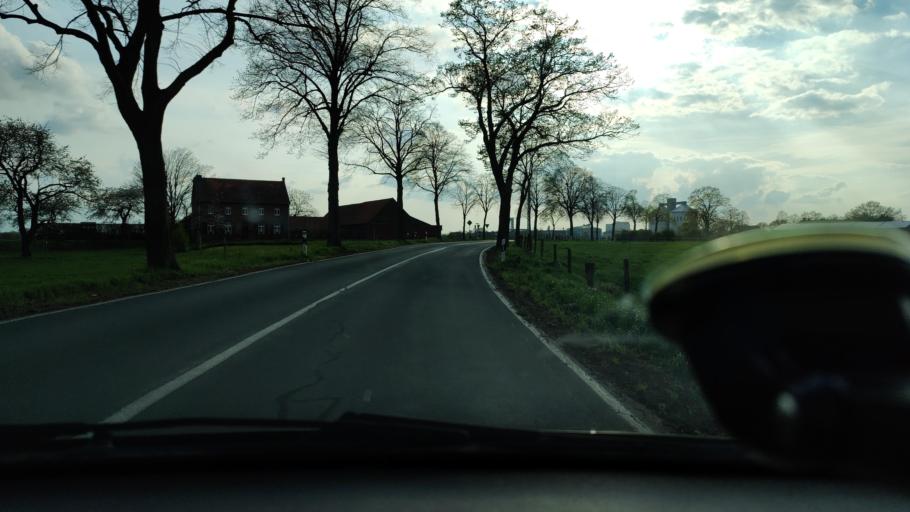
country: DE
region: North Rhine-Westphalia
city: Rees
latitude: 51.7321
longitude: 6.3754
